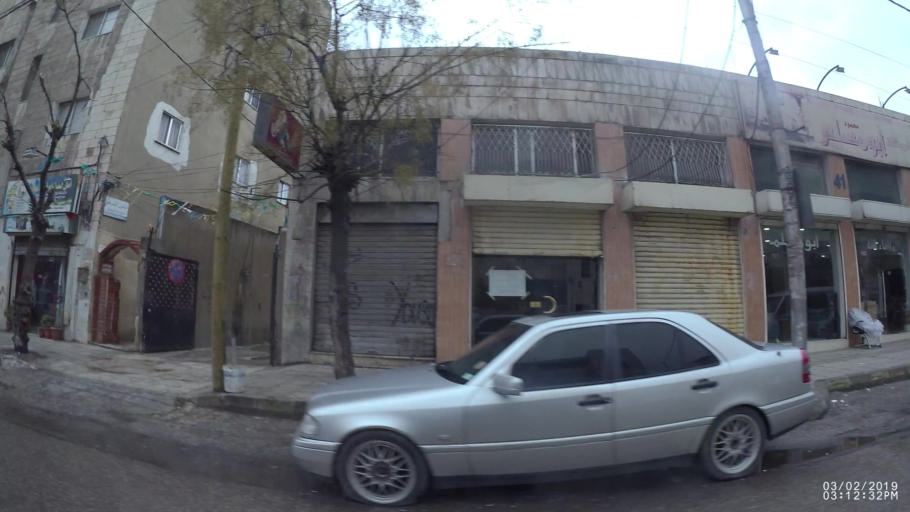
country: JO
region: Amman
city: Amman
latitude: 31.9605
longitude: 35.9299
